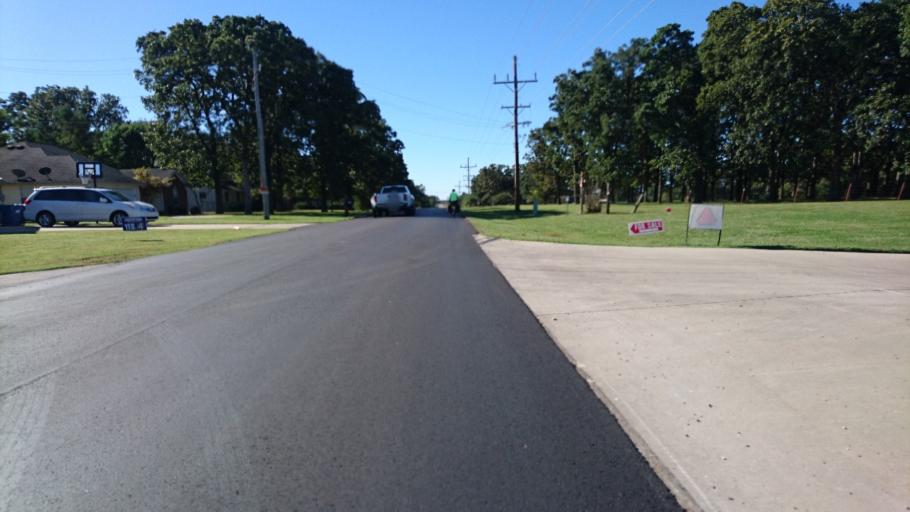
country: US
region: Missouri
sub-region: Jasper County
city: Joplin
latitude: 37.1172
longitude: -94.4939
